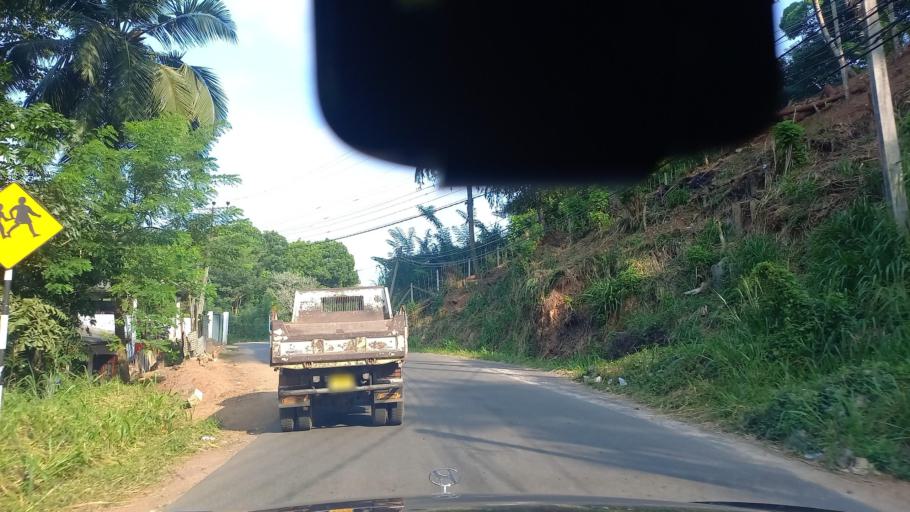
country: LK
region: Central
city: Kandy
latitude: 7.2353
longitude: 80.6027
